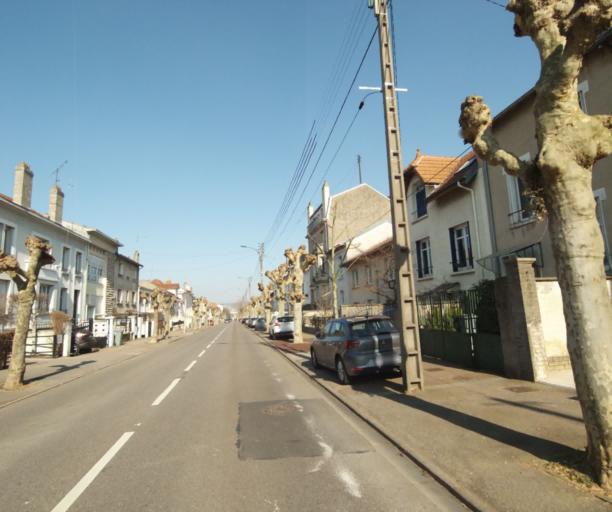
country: FR
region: Lorraine
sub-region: Departement de Meurthe-et-Moselle
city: Jarville-la-Malgrange
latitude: 48.6663
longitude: 6.1980
